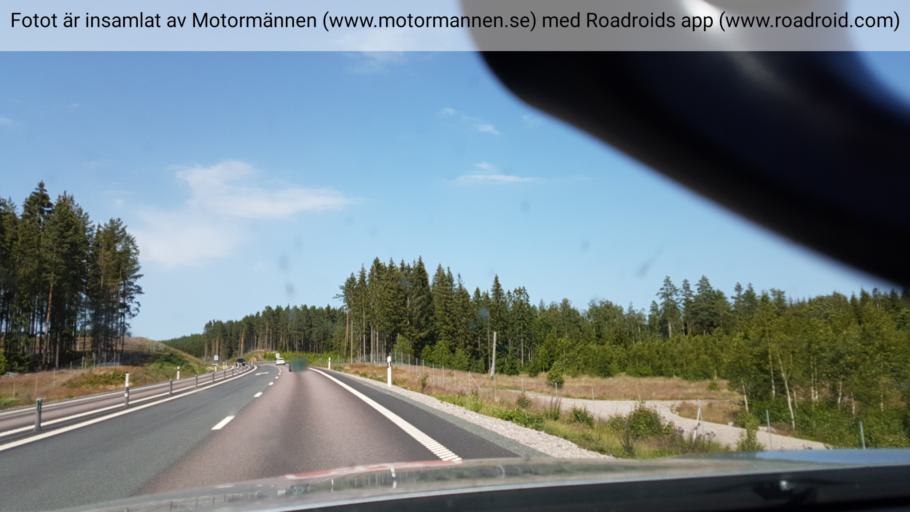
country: SE
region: Joenkoeping
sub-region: Aneby Kommun
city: Aneby
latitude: 57.8285
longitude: 14.8730
